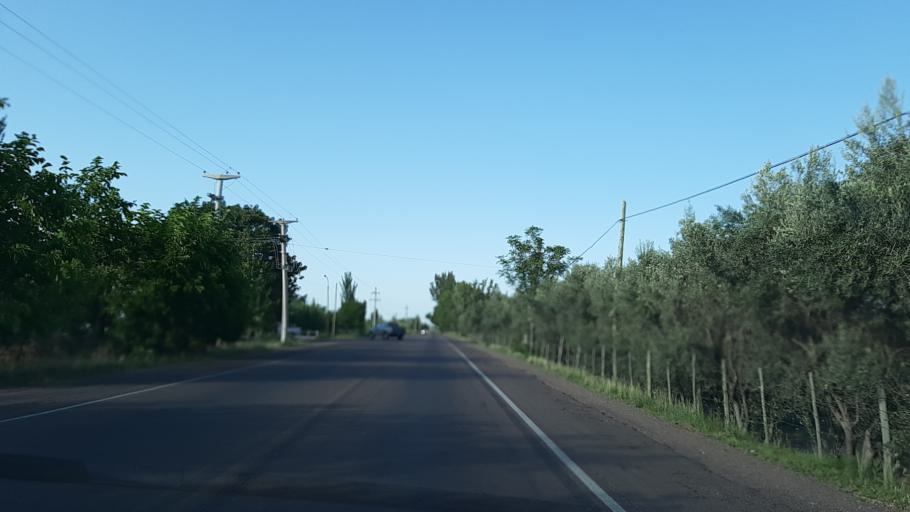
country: AR
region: Mendoza
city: San Martin
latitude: -32.9792
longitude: -68.4580
